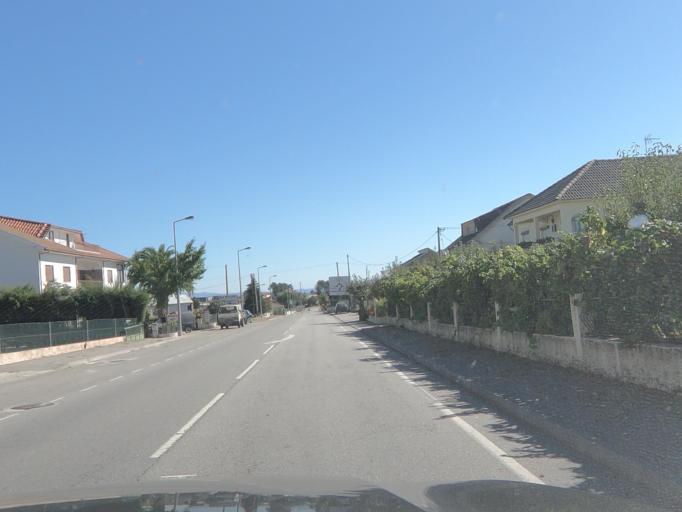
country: PT
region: Vila Real
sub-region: Valpacos
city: Valpacos
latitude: 41.6678
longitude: -7.3361
